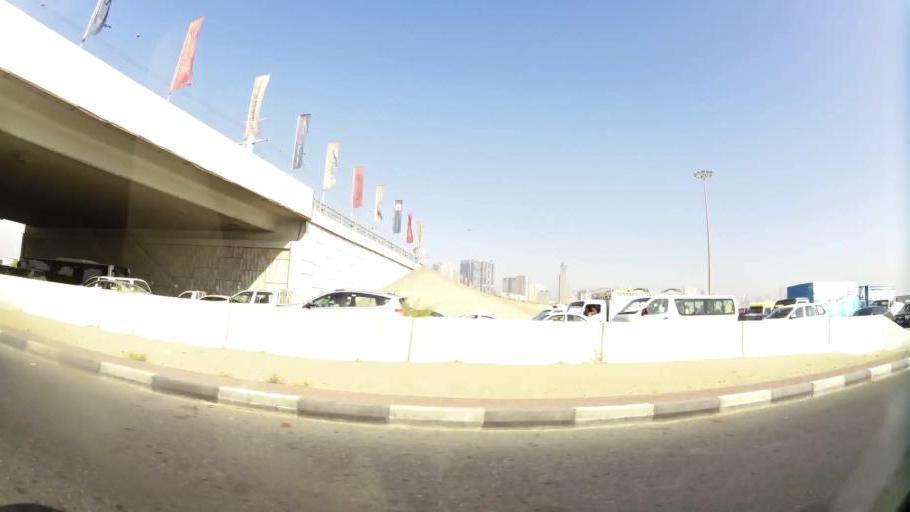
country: AE
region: Ash Shariqah
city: Sharjah
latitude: 25.2992
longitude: 55.3969
